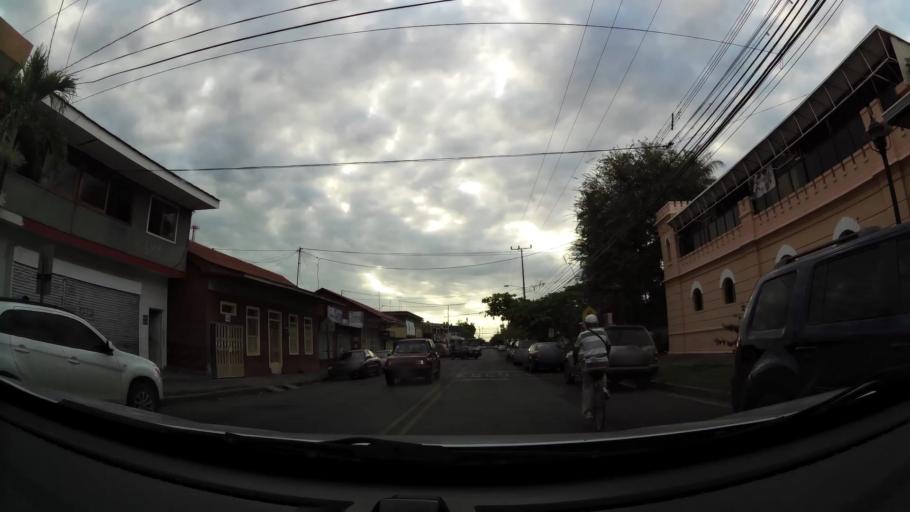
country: CR
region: Puntarenas
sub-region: Canton Central de Puntarenas
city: Puntarenas
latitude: 9.9773
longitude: -84.8340
